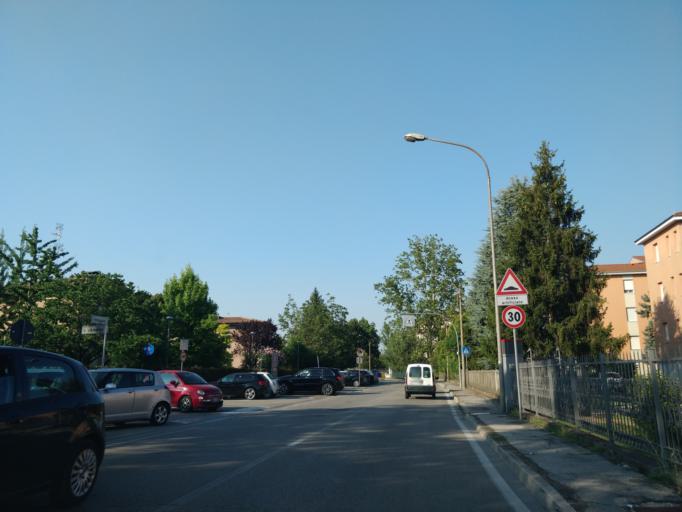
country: IT
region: Emilia-Romagna
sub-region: Provincia di Ferrara
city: Cento
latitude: 44.7255
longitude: 11.2932
